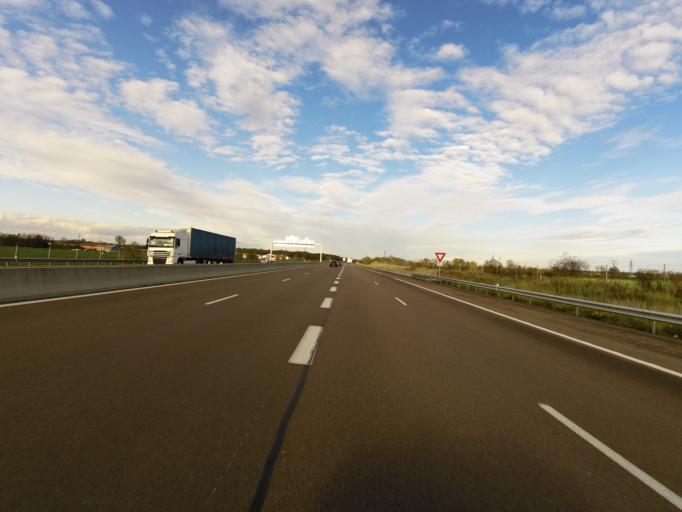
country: FR
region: Bourgogne
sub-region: Departement de la Cote-d'Or
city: Chevigny-Saint-Sauveur
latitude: 47.2839
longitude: 5.1553
